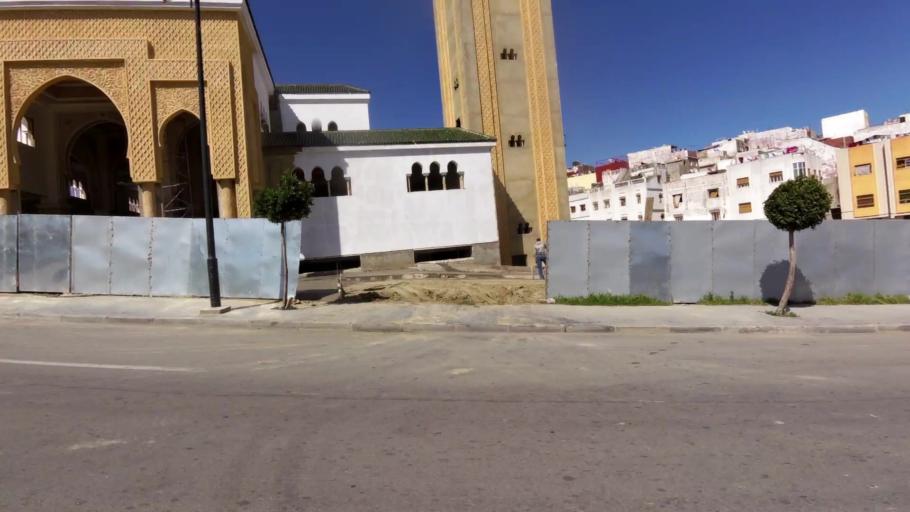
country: MA
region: Tanger-Tetouan
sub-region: Tanger-Assilah
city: Tangier
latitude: 35.7437
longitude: -5.8160
